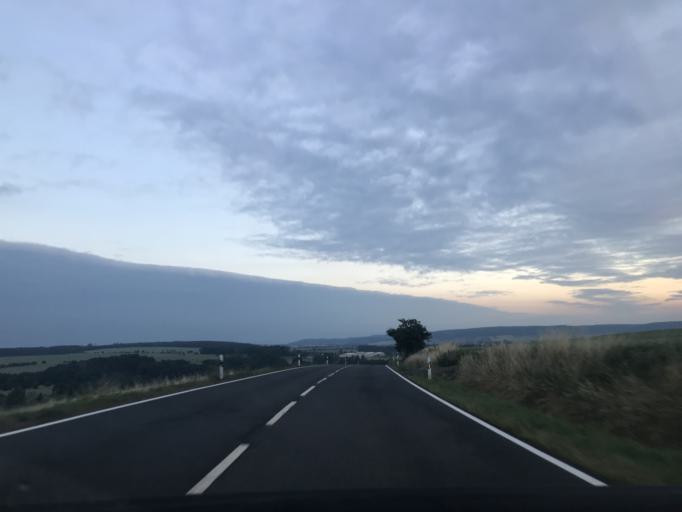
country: DE
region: Thuringia
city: Niederorschel
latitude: 51.3572
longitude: 10.4277
